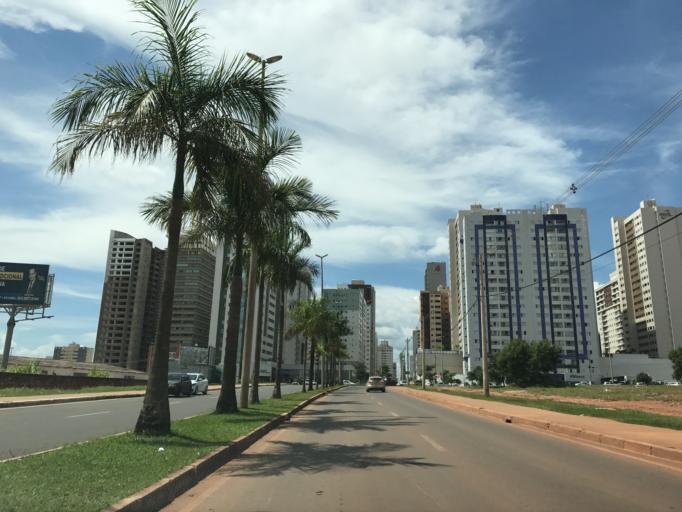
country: BR
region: Federal District
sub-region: Brasilia
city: Brasilia
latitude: -15.8346
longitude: -48.0423
